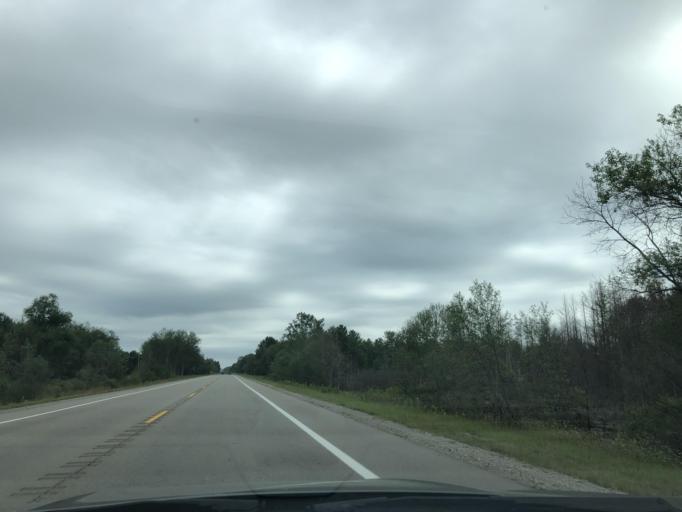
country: US
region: Michigan
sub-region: Clare County
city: Harrison
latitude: 44.0312
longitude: -85.0012
